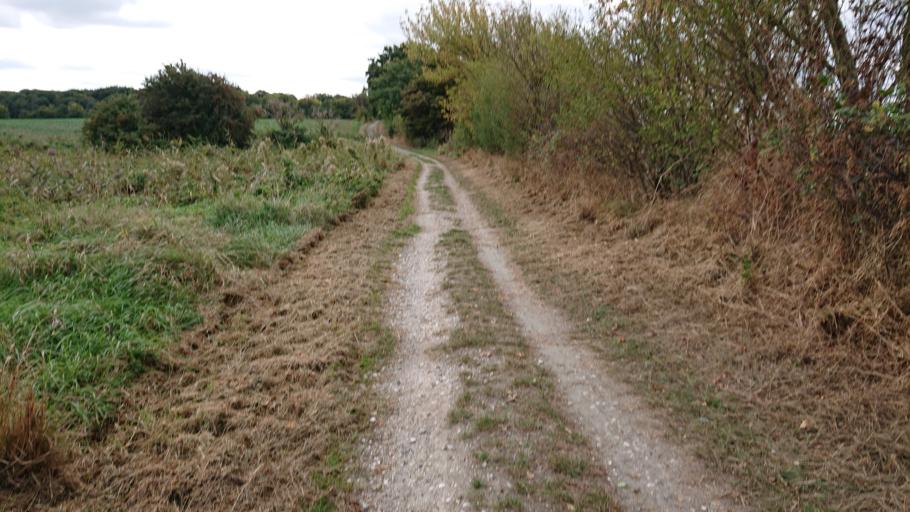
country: DE
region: Mecklenburg-Vorpommern
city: Altefahr
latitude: 54.3370
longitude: 13.1146
